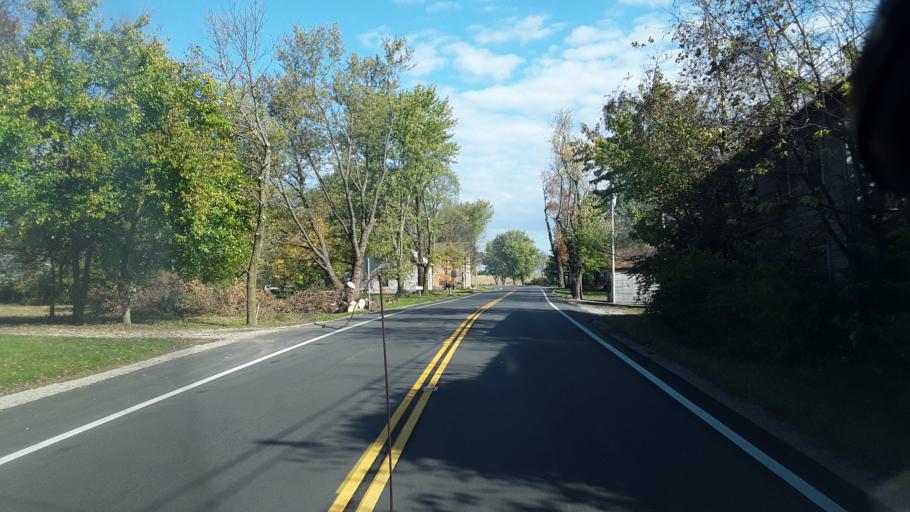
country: US
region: Ohio
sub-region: Highland County
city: Leesburg
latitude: 39.2838
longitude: -83.5924
